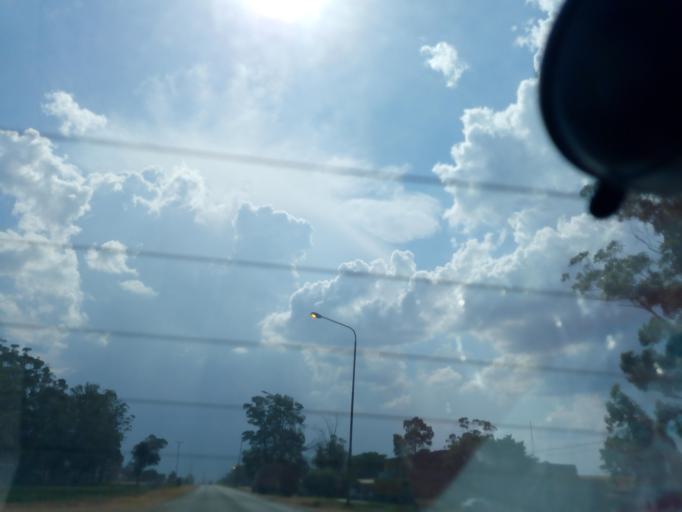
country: AR
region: Corrientes
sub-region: Departamento de Paso de los Libres
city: Paso de los Libres
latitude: -29.7219
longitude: -57.1264
